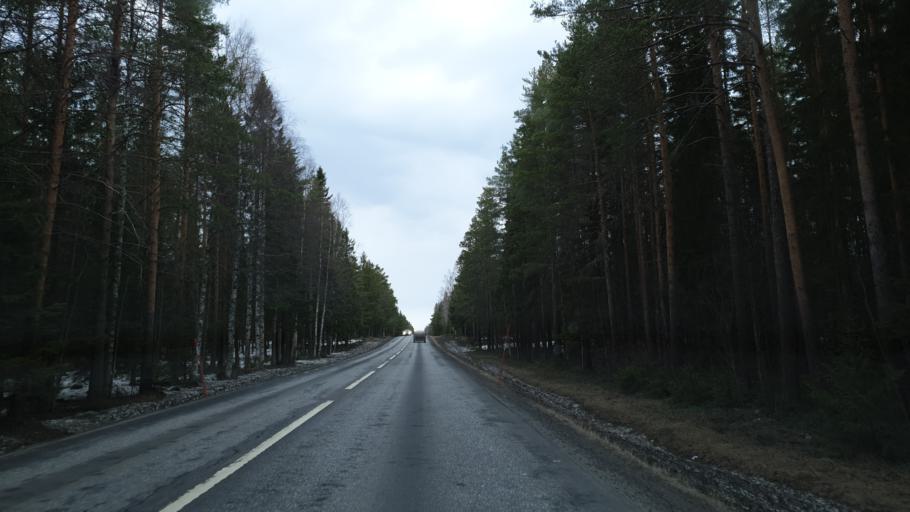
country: SE
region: Vaesterbotten
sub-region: Skelleftea Kommun
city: Viken
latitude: 64.6544
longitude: 20.9544
